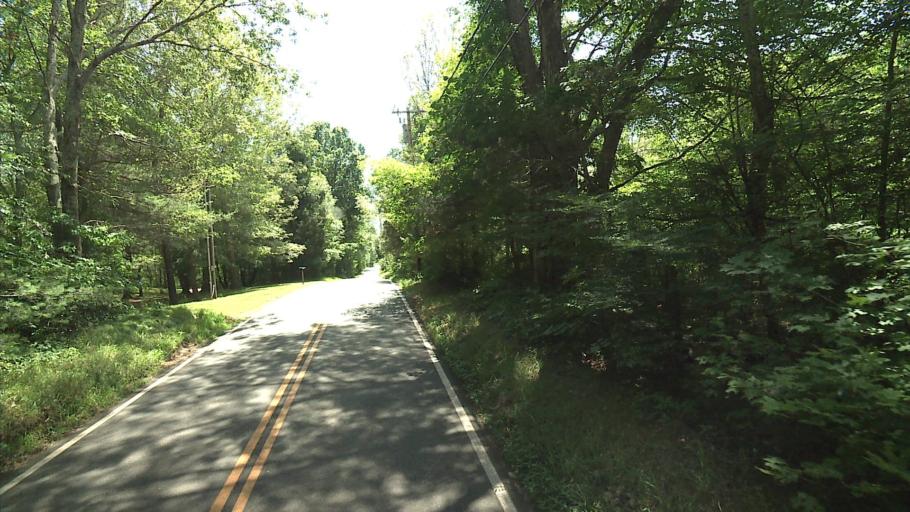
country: US
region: Connecticut
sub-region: Middlesex County
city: Essex Village
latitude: 41.4405
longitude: -72.3382
